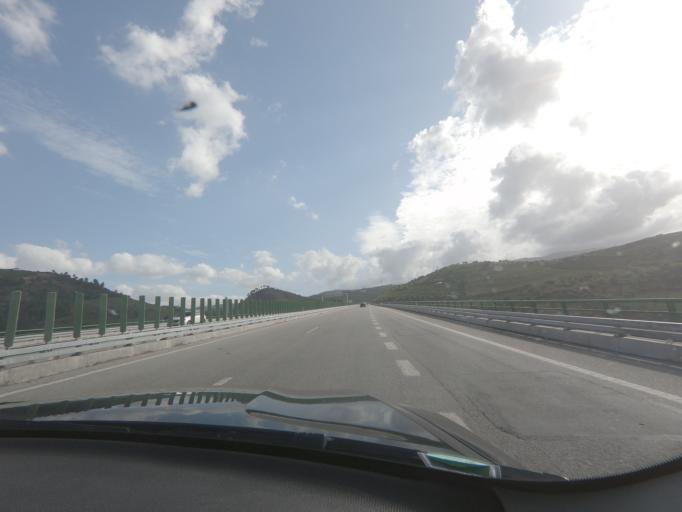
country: PT
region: Vila Real
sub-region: Peso da Regua
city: Peso da Regua
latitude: 41.1325
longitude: -7.7728
